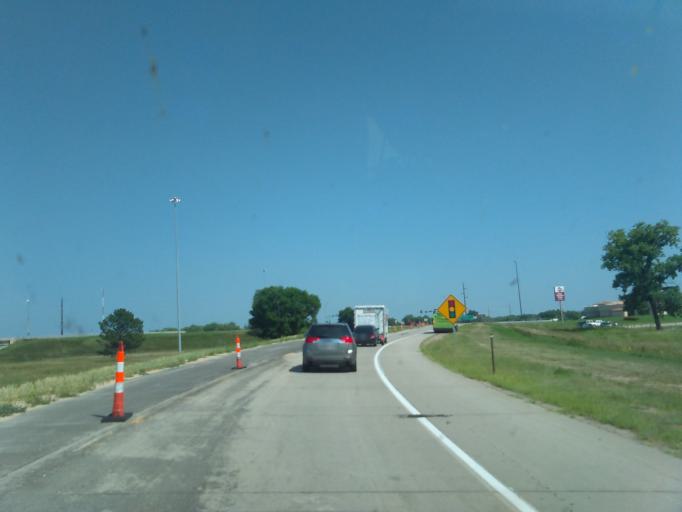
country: US
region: Nebraska
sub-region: Buffalo County
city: Kearney
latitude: 40.6690
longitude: -99.0889
